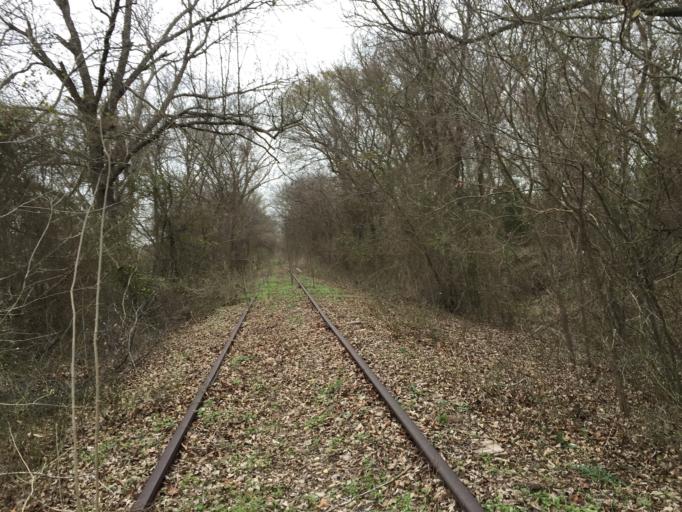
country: US
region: Texas
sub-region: Bell County
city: Belton
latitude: 31.0466
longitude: -97.4235
